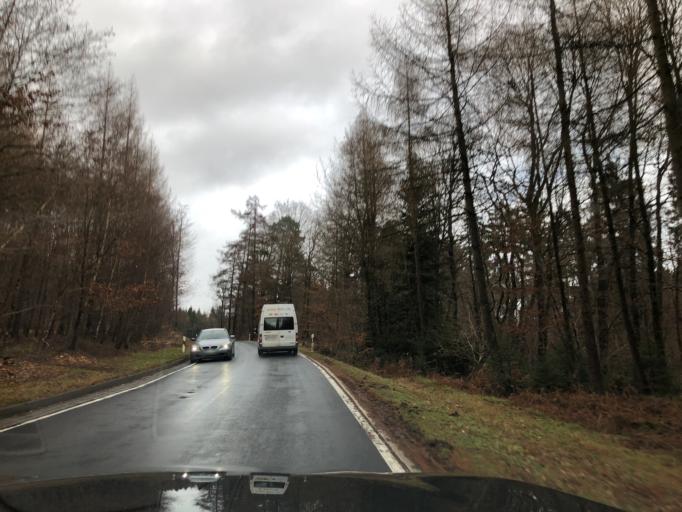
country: DE
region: Rheinland-Pfalz
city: Ockenfels
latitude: 50.6160
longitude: 7.3013
